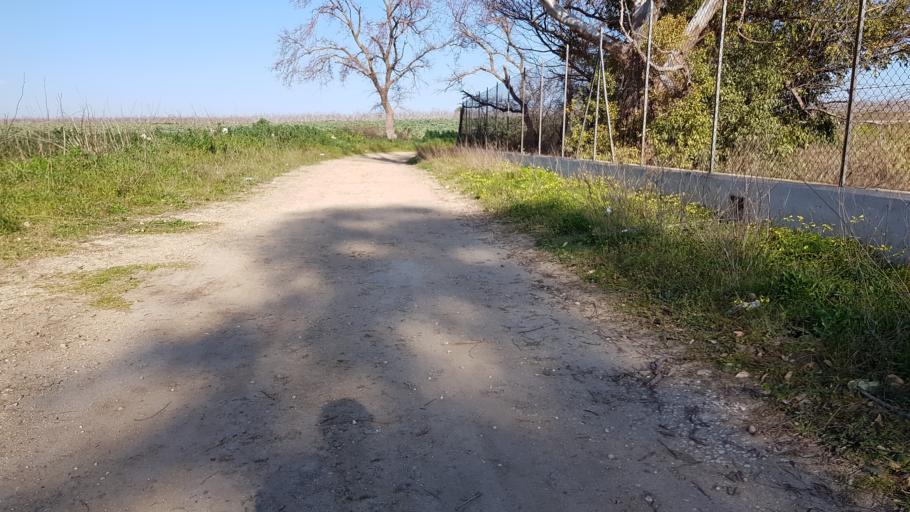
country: IT
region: Apulia
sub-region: Provincia di Brindisi
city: Brindisi
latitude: 40.6260
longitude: 17.8932
